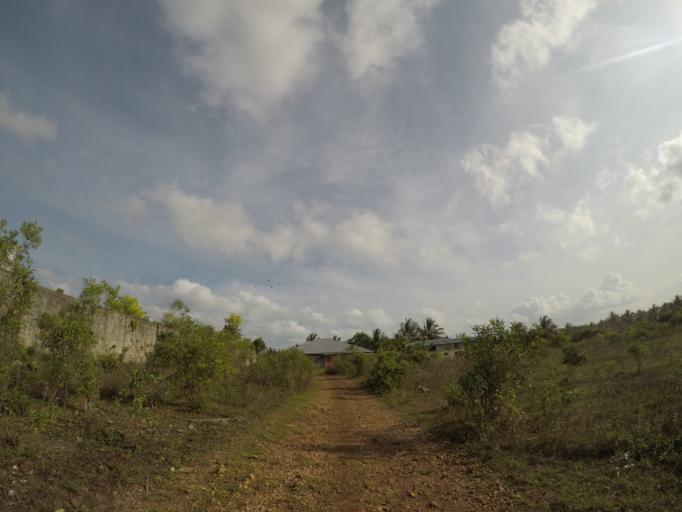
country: TZ
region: Zanzibar Central/South
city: Koani
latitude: -6.2242
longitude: 39.3085
